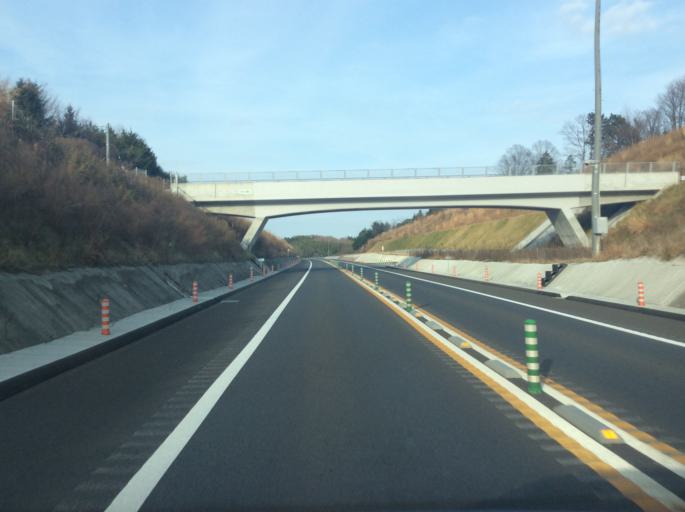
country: JP
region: Fukushima
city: Namie
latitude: 37.4554
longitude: 140.9615
